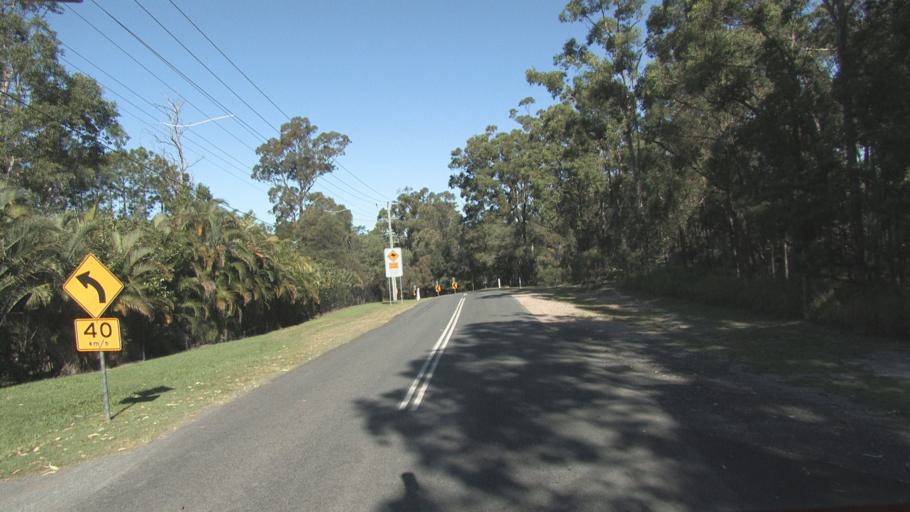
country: AU
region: Queensland
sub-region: Logan
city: Springwood
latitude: -27.6054
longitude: 153.1730
